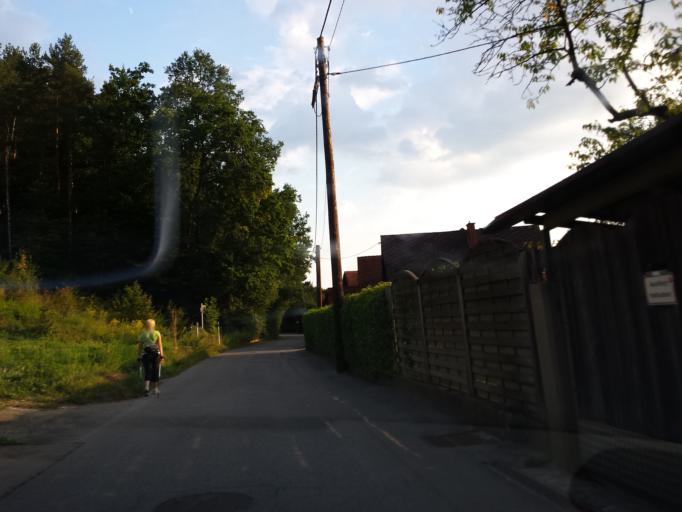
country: AT
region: Styria
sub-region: Politischer Bezirk Graz-Umgebung
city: Stattegg
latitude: 47.1228
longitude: 15.4294
